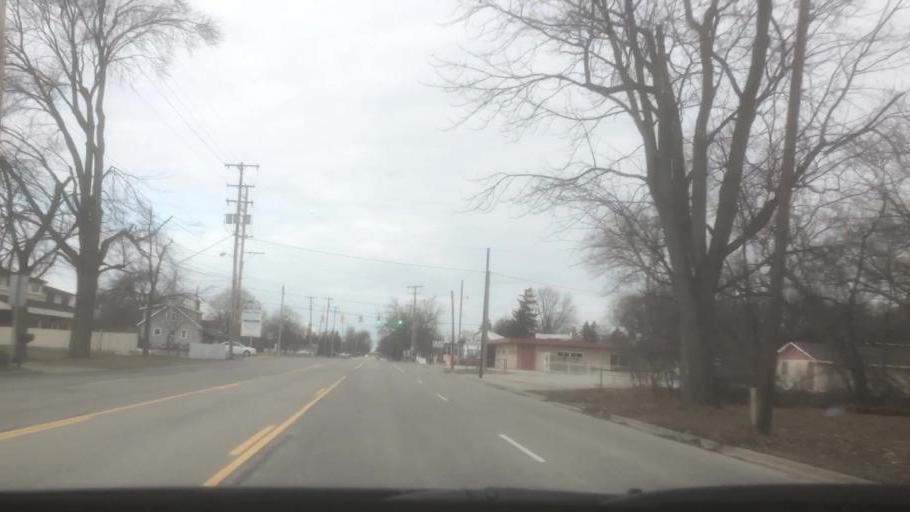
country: US
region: Michigan
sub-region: Bay County
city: Bay City
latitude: 43.6022
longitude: -83.9309
